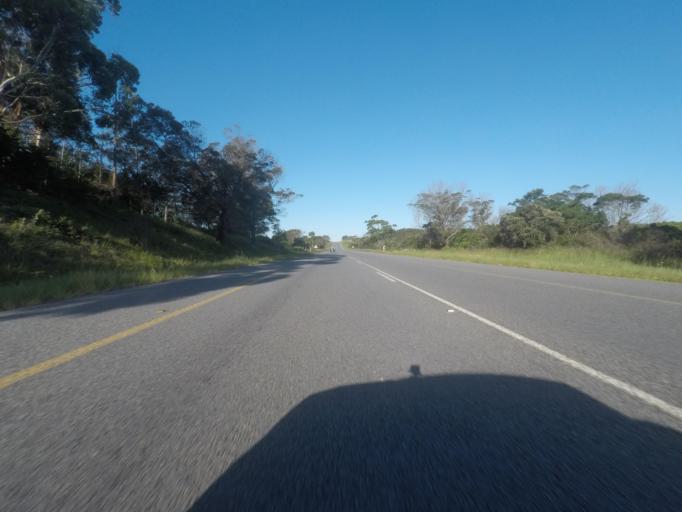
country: ZA
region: Eastern Cape
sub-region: Buffalo City Metropolitan Municipality
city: East London
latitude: -33.0599
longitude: 27.7908
